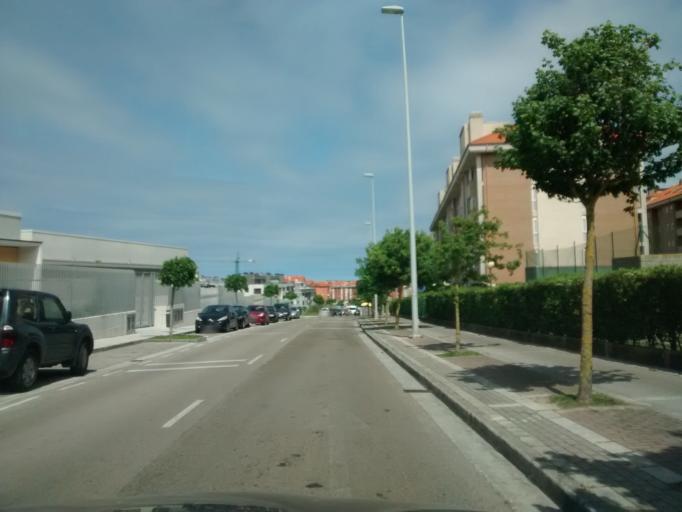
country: ES
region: Cantabria
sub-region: Provincia de Cantabria
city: Santander
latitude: 43.4792
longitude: -3.8020
